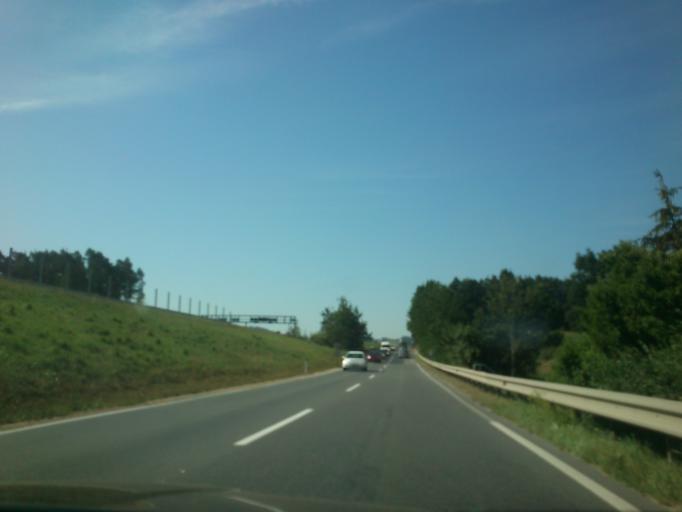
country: AT
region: Upper Austria
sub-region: Politischer Bezirk Freistadt
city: Freistadt
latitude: 48.4615
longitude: 14.5015
